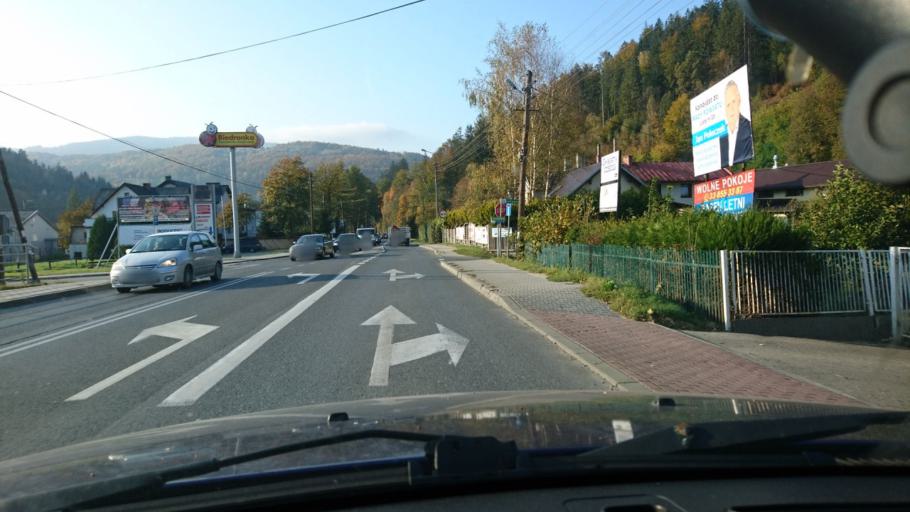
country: PL
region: Silesian Voivodeship
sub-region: Powiat cieszynski
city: Wisla
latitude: 49.6633
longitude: 18.8528
